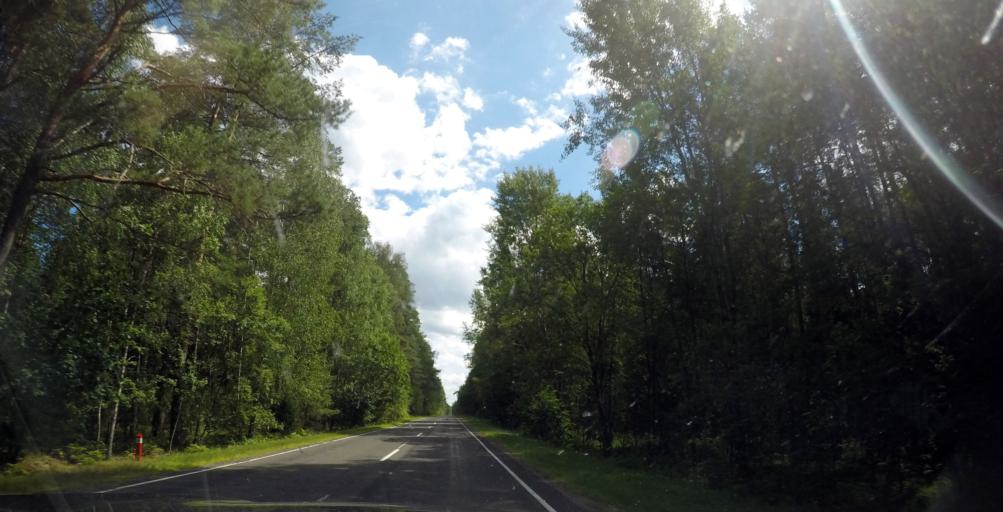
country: BY
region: Grodnenskaya
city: Skidal'
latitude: 53.8459
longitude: 24.2049
